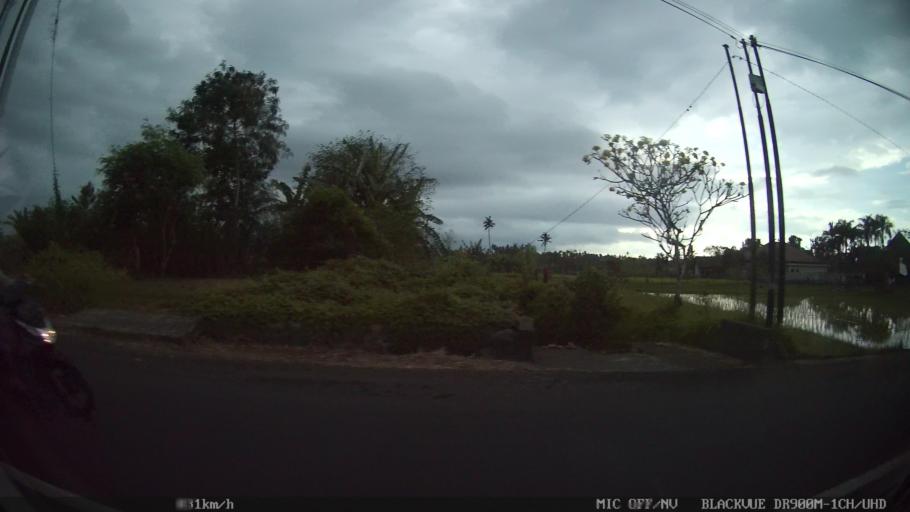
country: ID
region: Bali
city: Banjar Pasekan
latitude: -8.6162
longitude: 115.2980
